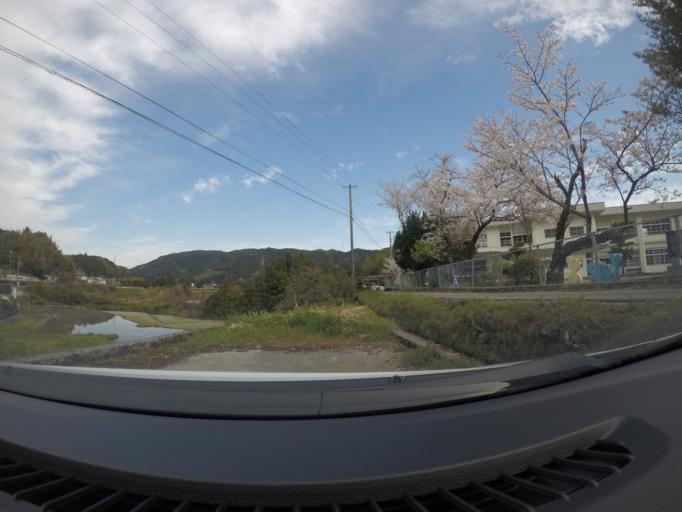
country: JP
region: Kochi
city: Kochi-shi
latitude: 33.6389
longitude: 133.7184
